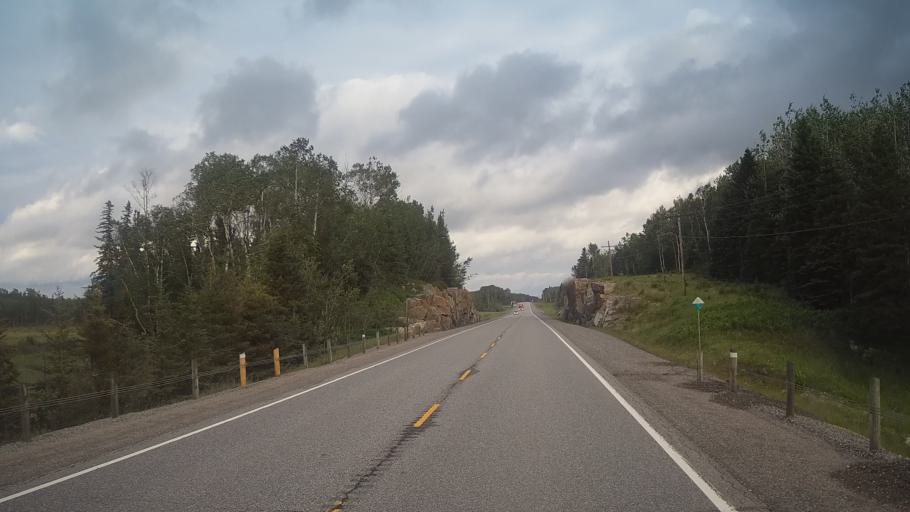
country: CA
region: Ontario
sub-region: Rainy River District
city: Atikokan
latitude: 49.0132
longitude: -90.4288
